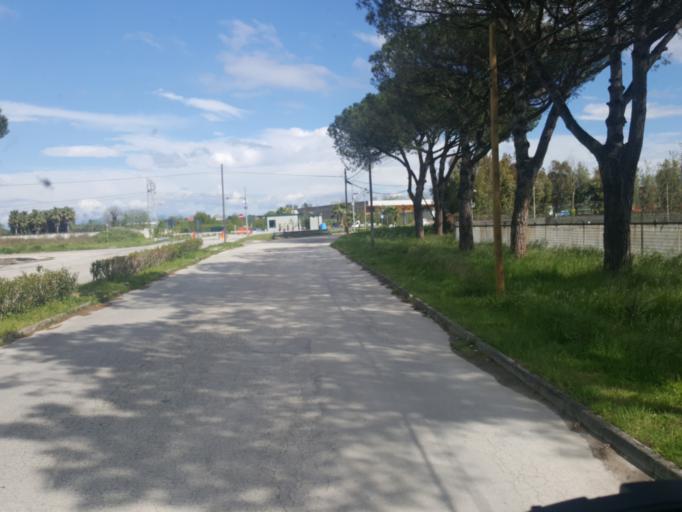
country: IT
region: Campania
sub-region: Provincia di Napoli
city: Torretta-Scalzapecora
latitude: 40.9342
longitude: 14.1210
